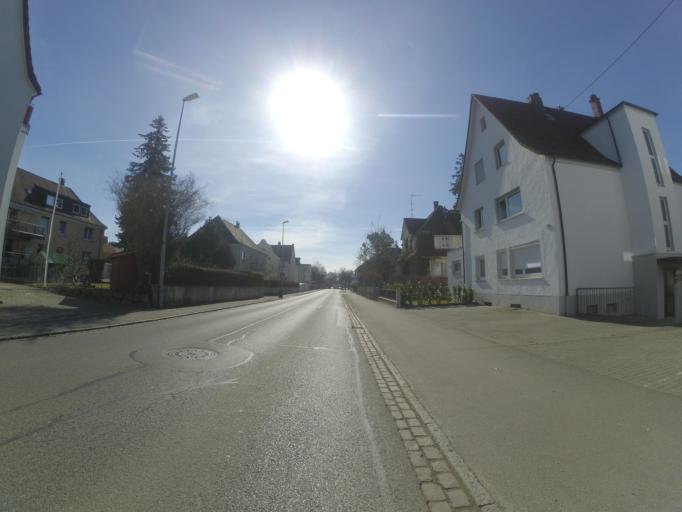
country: DE
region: Baden-Wuerttemberg
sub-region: Tuebingen Region
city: Ravensburg
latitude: 47.7728
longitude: 9.6081
